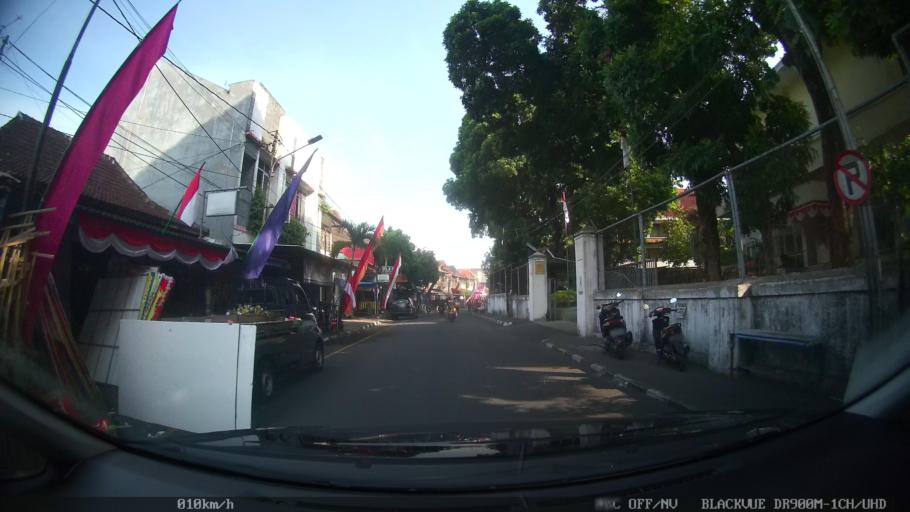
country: ID
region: Daerah Istimewa Yogyakarta
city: Yogyakarta
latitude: -7.7893
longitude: 110.3695
